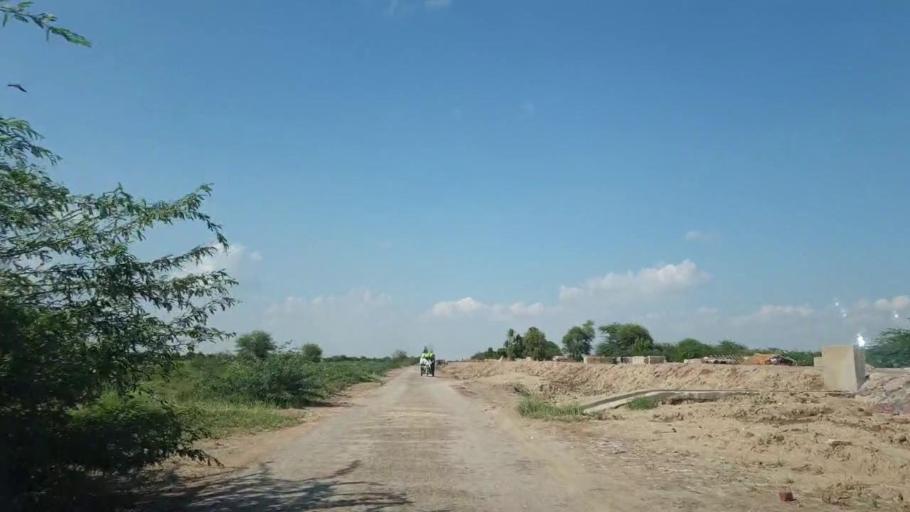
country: PK
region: Sindh
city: Pithoro
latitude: 25.6265
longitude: 69.4320
